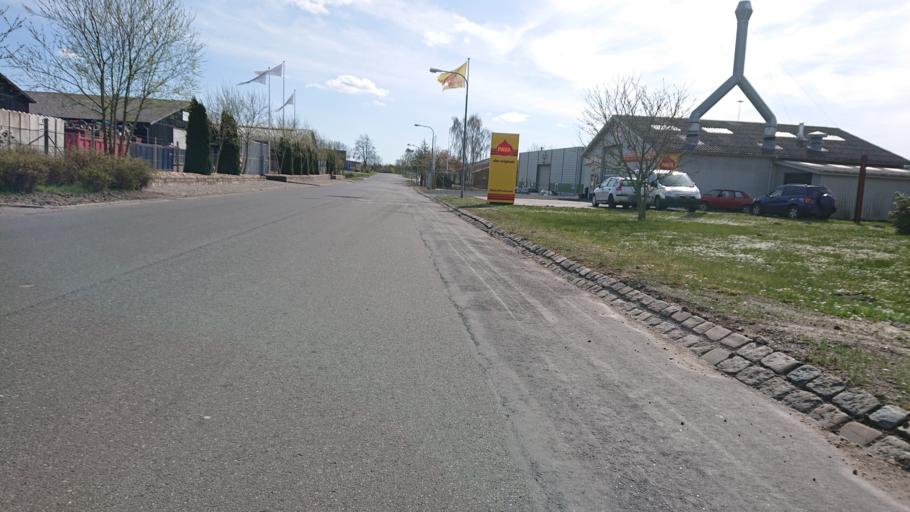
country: DK
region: South Denmark
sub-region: Nyborg Kommune
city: Nyborg
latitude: 55.3130
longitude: 10.7523
